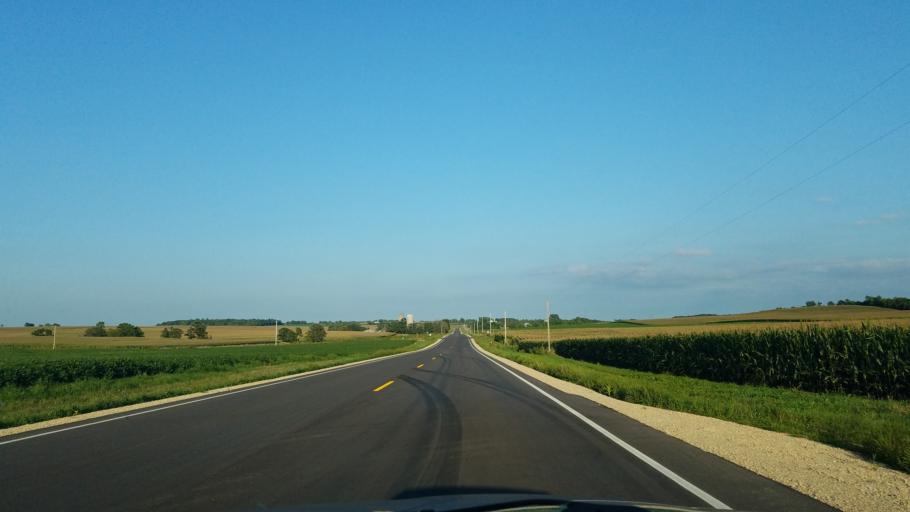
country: US
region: Wisconsin
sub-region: Saint Croix County
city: Hammond
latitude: 45.0791
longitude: -92.3989
